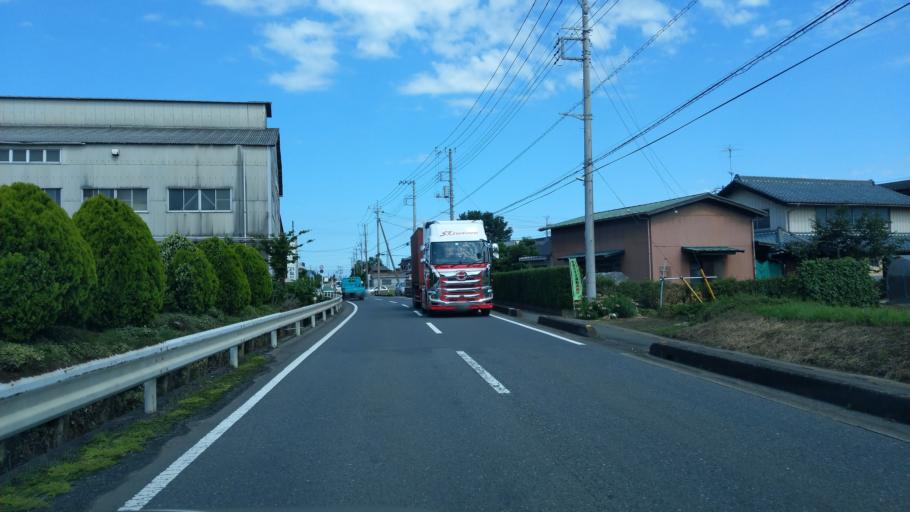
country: JP
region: Saitama
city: Okegawa
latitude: 35.9772
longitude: 139.4926
